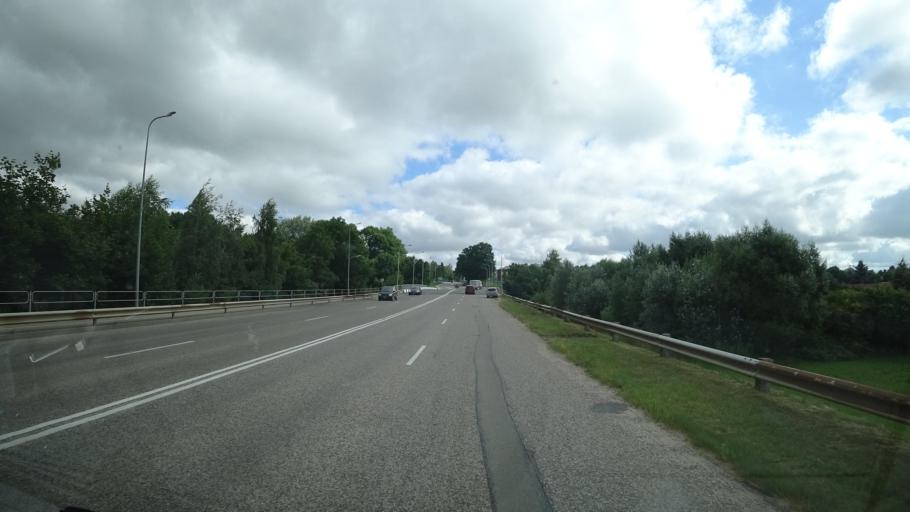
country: LT
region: Marijampoles apskritis
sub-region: Marijampole Municipality
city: Marijampole
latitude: 54.5360
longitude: 23.3379
